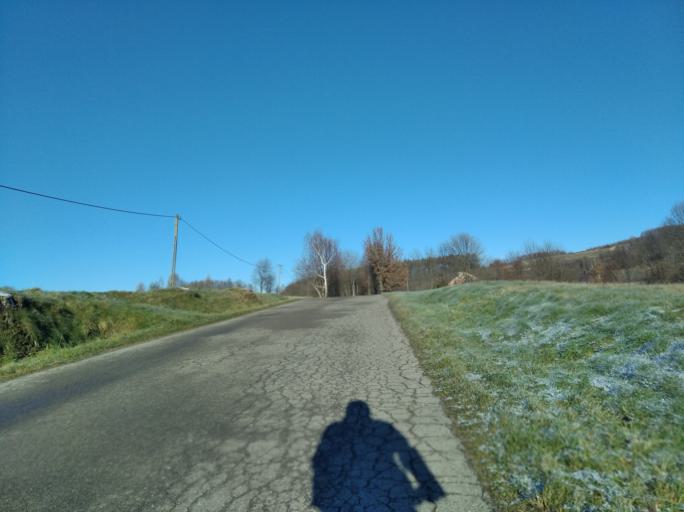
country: PL
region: Subcarpathian Voivodeship
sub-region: Powiat strzyzowski
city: Czudec
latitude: 49.9412
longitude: 21.7877
